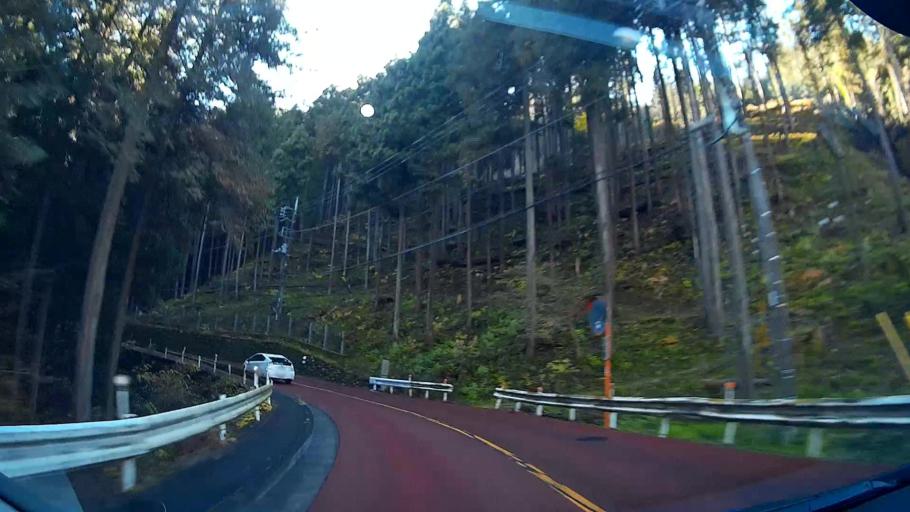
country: JP
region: Tokyo
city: Itsukaichi
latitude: 35.7218
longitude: 139.1466
